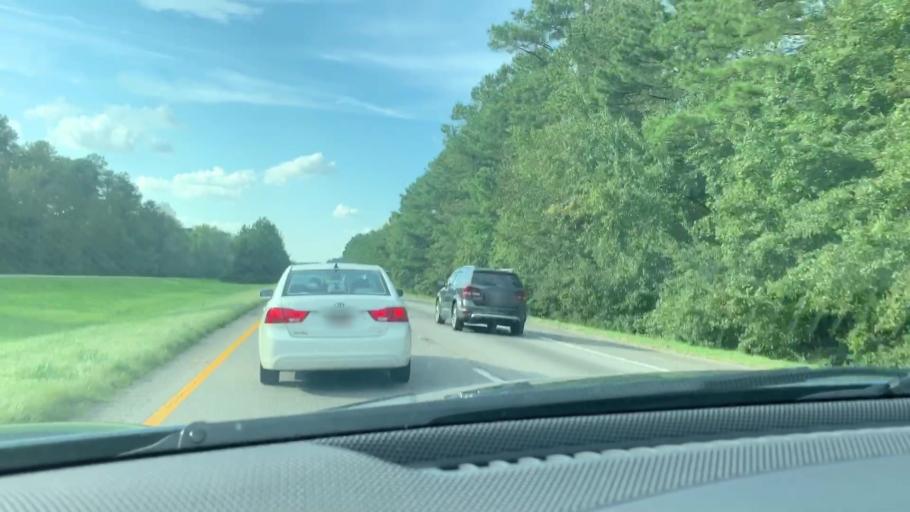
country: US
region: South Carolina
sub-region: Orangeburg County
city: Brookdale
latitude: 33.4434
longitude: -80.7106
